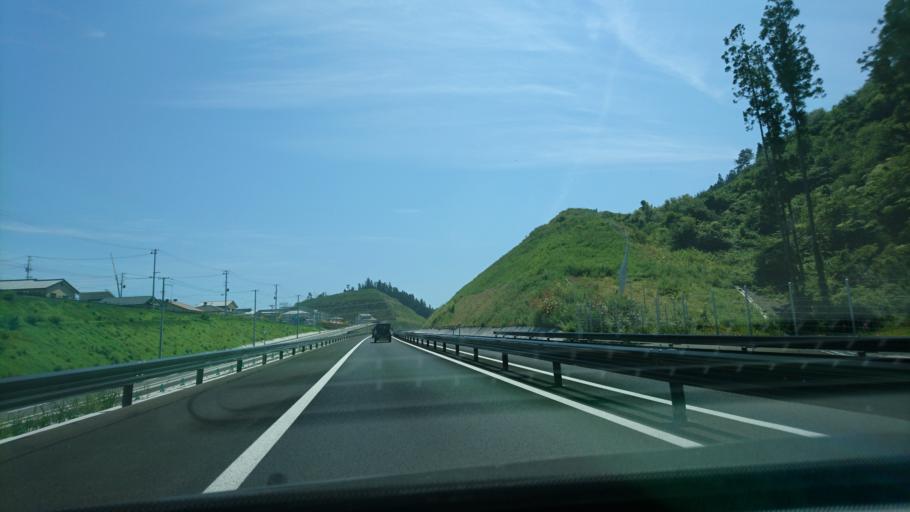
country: JP
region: Iwate
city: Ofunato
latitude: 39.0039
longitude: 141.6131
